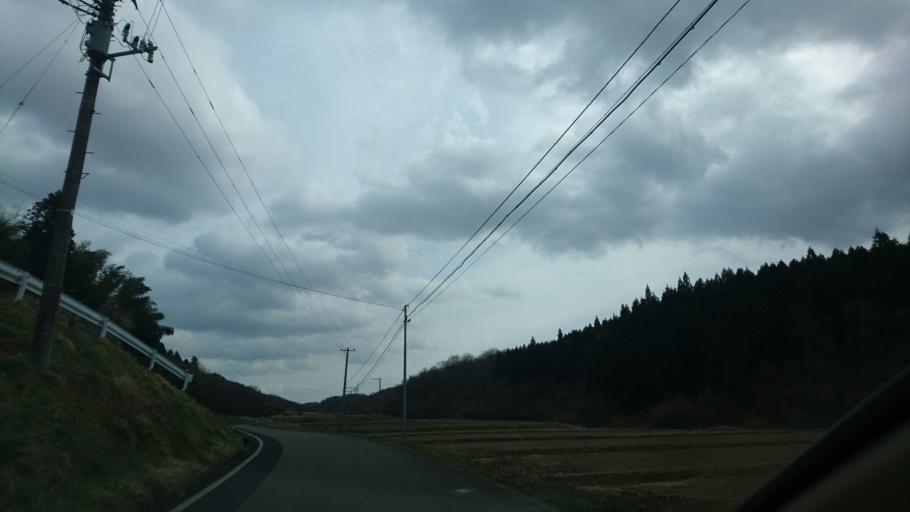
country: JP
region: Iwate
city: Ichinoseki
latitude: 38.8990
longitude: 141.1813
